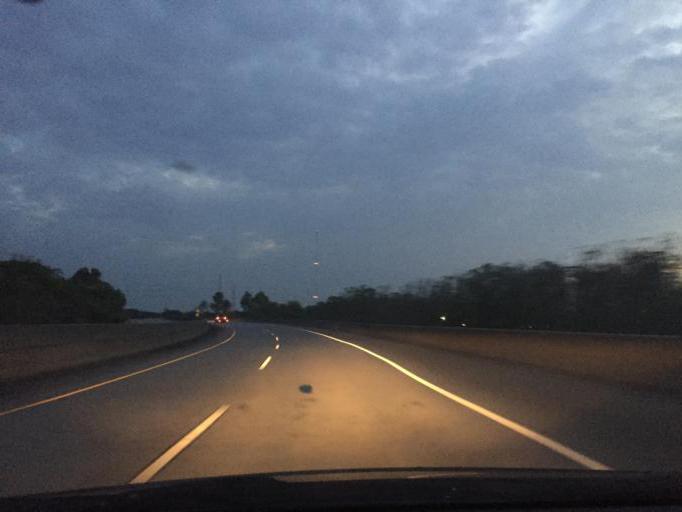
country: US
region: Georgia
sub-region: Chatham County
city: Savannah
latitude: 32.0705
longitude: -81.0739
